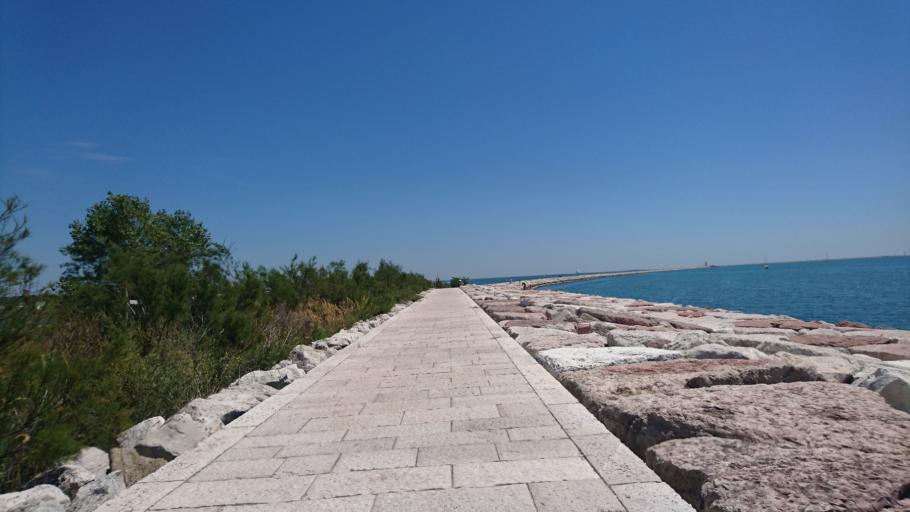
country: IT
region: Veneto
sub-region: Provincia di Venezia
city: Lido
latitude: 45.4274
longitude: 12.4109
